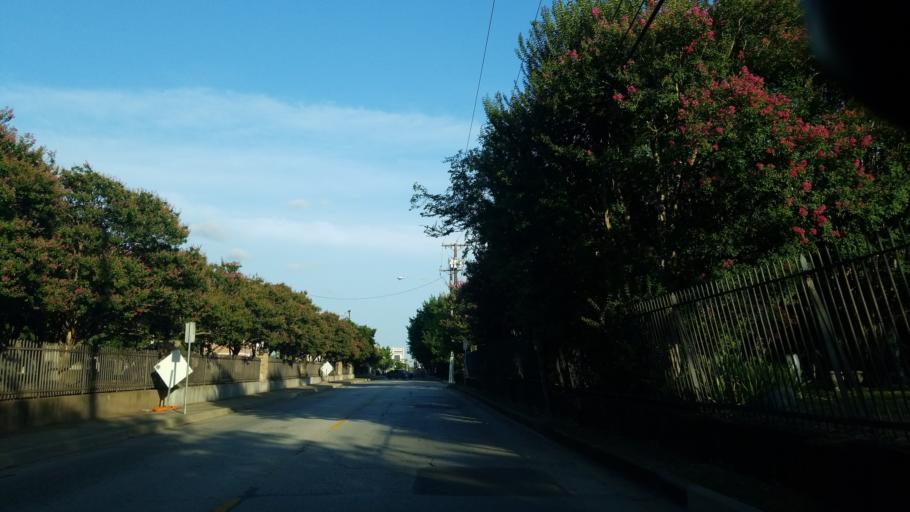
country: US
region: Texas
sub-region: Dallas County
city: Dallas
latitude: 32.8014
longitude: -96.7962
